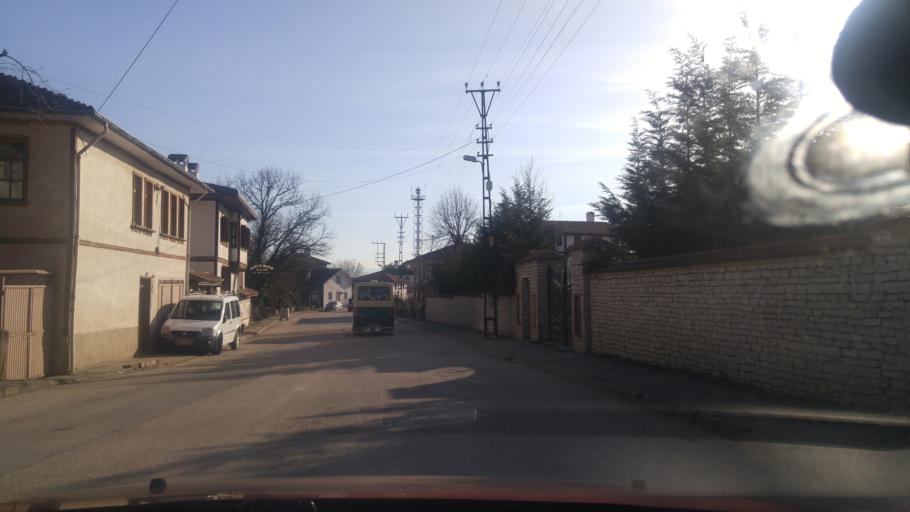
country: TR
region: Karabuk
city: Safranbolu
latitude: 41.2648
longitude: 32.6706
